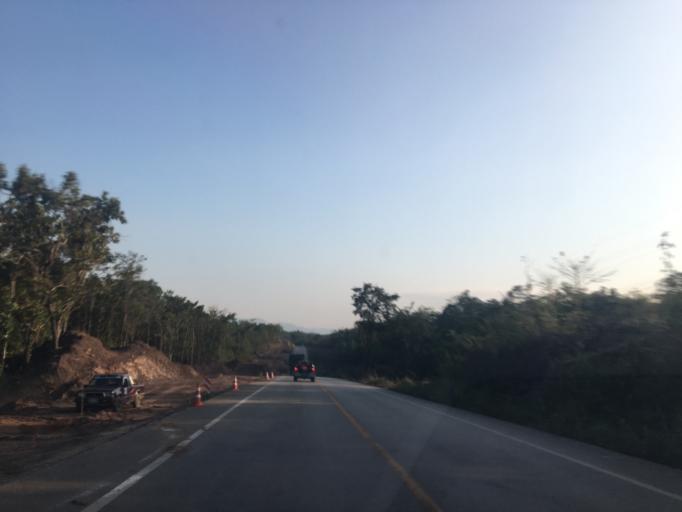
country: TH
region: Lampang
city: Ngao
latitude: 18.6834
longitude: 100.0050
